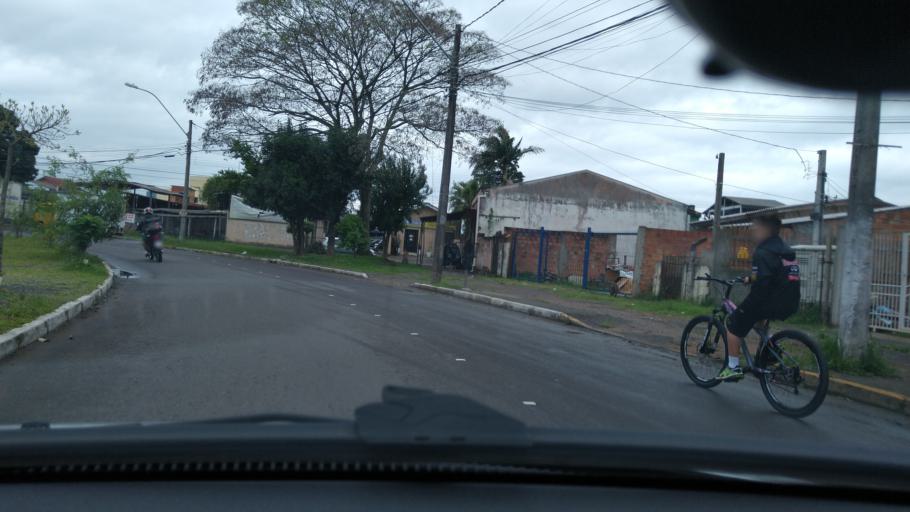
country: BR
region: Rio Grande do Sul
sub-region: Canoas
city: Canoas
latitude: -29.9027
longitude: -51.2038
